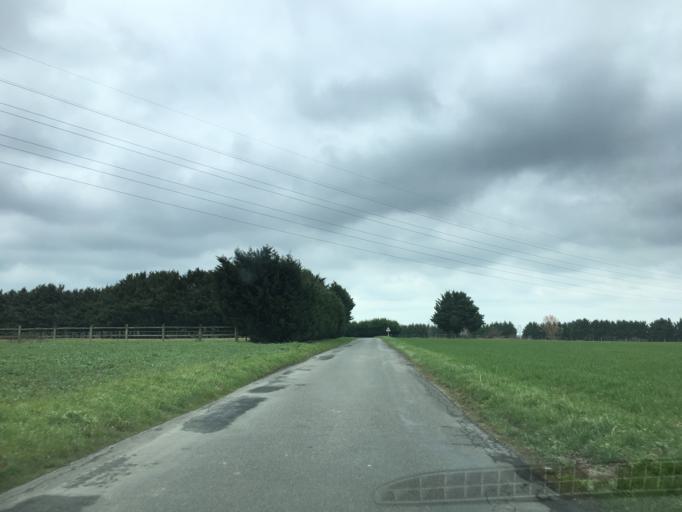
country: FR
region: Centre
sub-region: Departement d'Indre-et-Loire
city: Chanceaux-sur-Choisille
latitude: 47.4695
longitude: 0.6856
